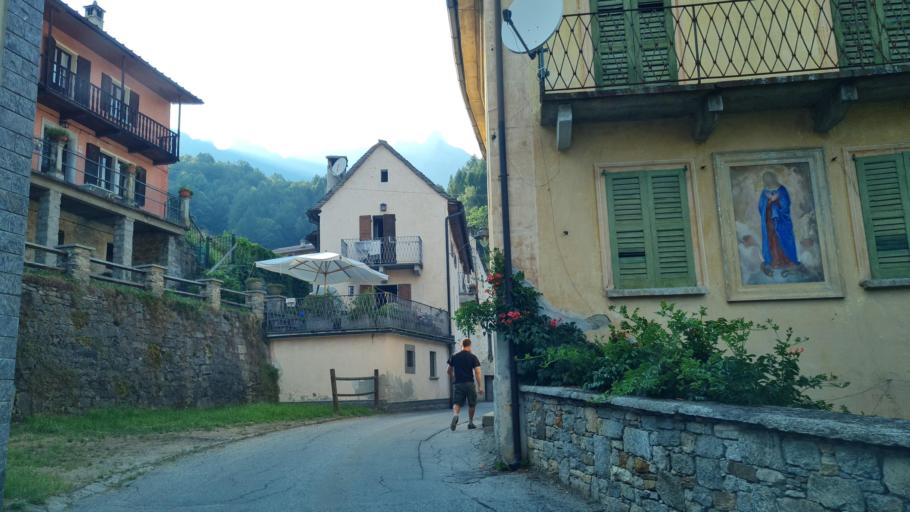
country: IT
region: Piedmont
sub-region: Provincia Verbano-Cusio-Ossola
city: Crodo
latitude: 46.2237
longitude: 8.3086
